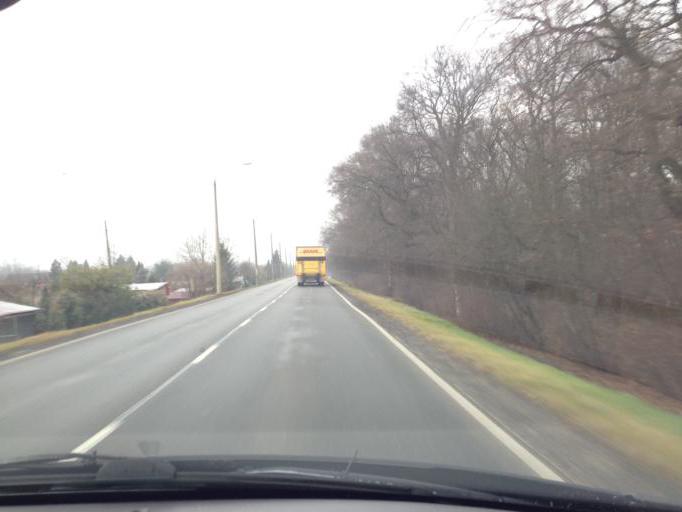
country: PL
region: Lesser Poland Voivodeship
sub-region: Powiat wielicki
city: Kokotow
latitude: 50.0533
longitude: 20.0575
